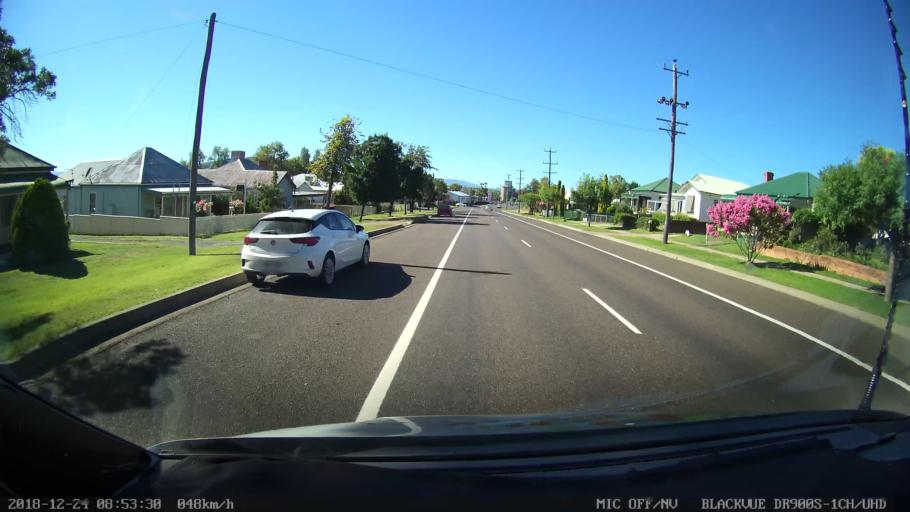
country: AU
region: New South Wales
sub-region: Liverpool Plains
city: Quirindi
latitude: -31.4990
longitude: 150.6812
